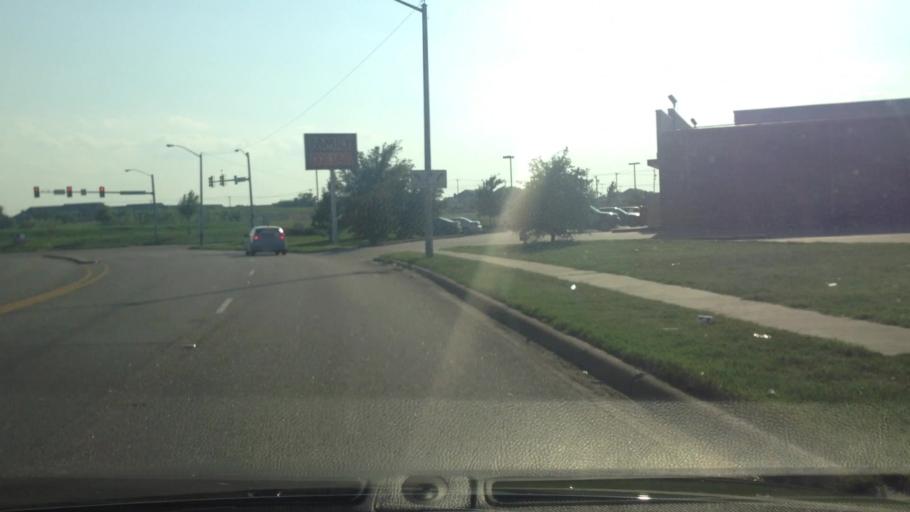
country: US
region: Texas
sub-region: Tarrant County
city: Edgecliff Village
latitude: 32.6348
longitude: -97.3449
